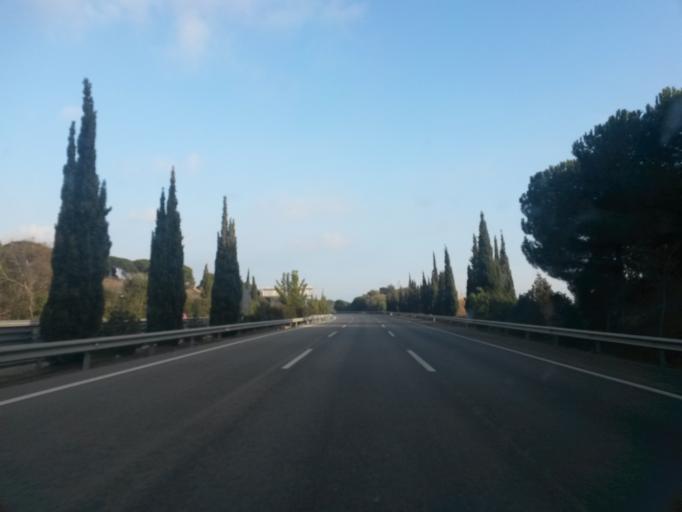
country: ES
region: Catalonia
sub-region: Provincia de Barcelona
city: Canet de Mar
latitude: 41.5998
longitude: 2.5833
